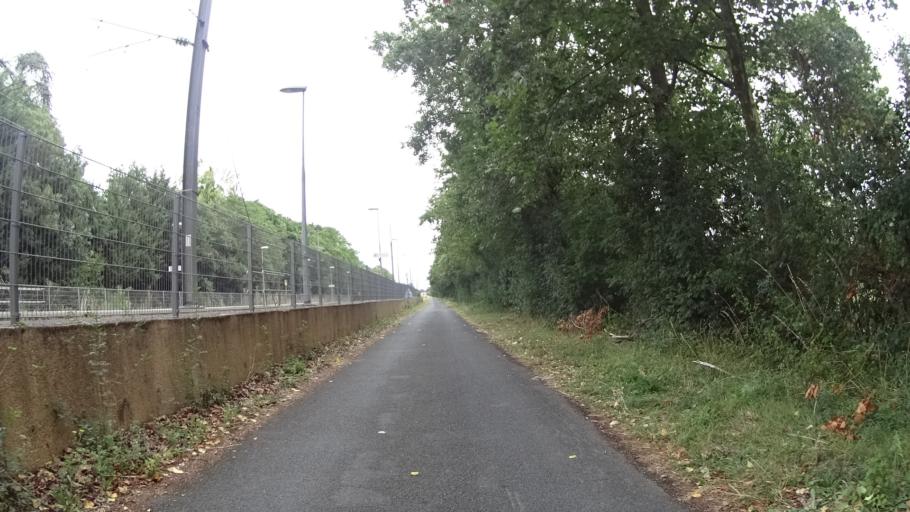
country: FR
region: Pays de la Loire
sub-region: Departement de Maine-et-Loire
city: Savennieres
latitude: 47.3815
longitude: -0.6545
